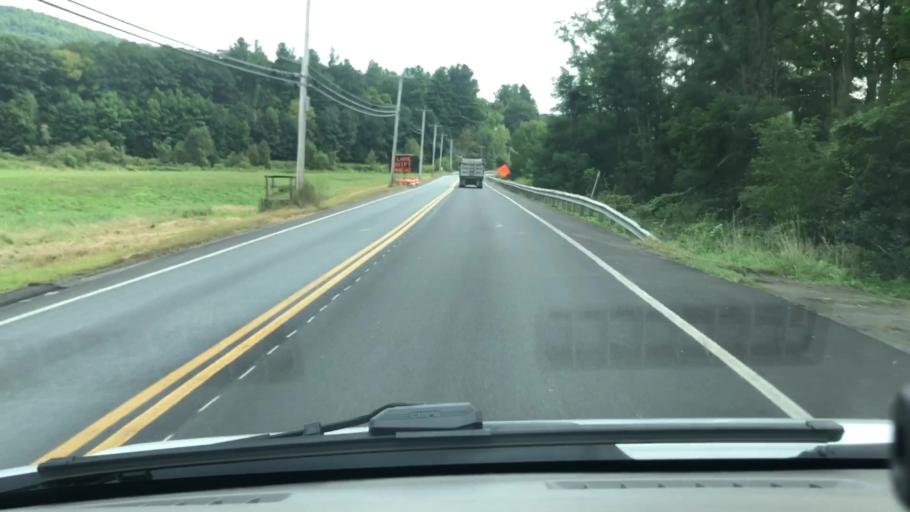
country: US
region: Massachusetts
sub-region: Franklin County
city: Buckland
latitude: 42.6210
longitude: -72.7735
